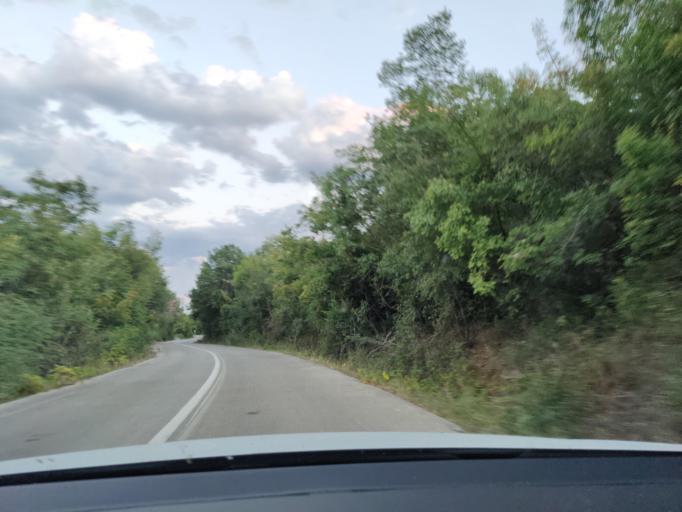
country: GR
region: Central Macedonia
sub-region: Nomos Serron
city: Chrysochorafa
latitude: 41.1659
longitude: 23.1812
